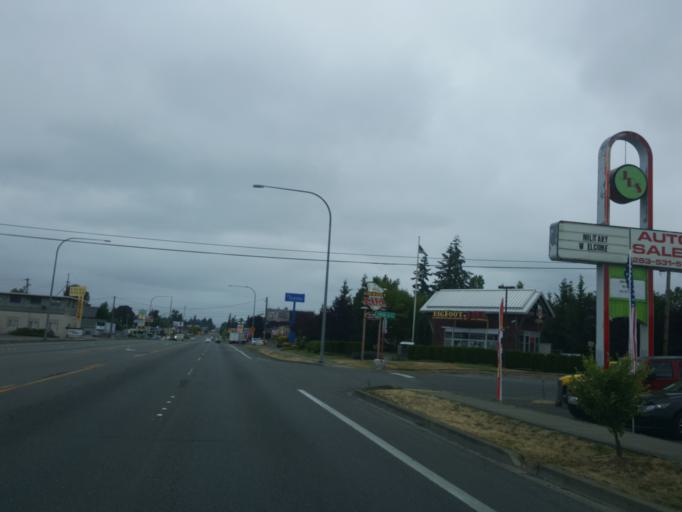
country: US
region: Washington
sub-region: Pierce County
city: Parkland
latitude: 47.1329
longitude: -122.4346
